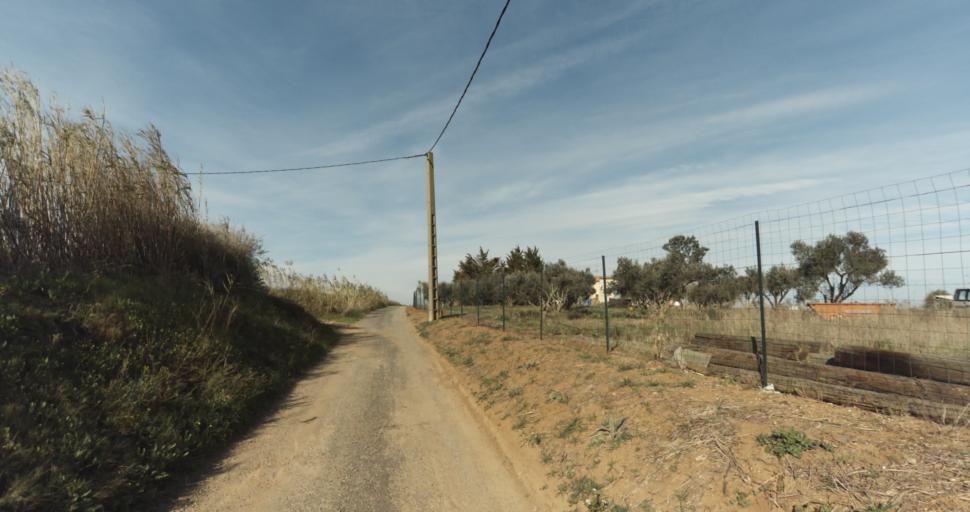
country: FR
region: Languedoc-Roussillon
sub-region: Departement de l'Herault
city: Marseillan
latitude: 43.3599
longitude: 3.5160
